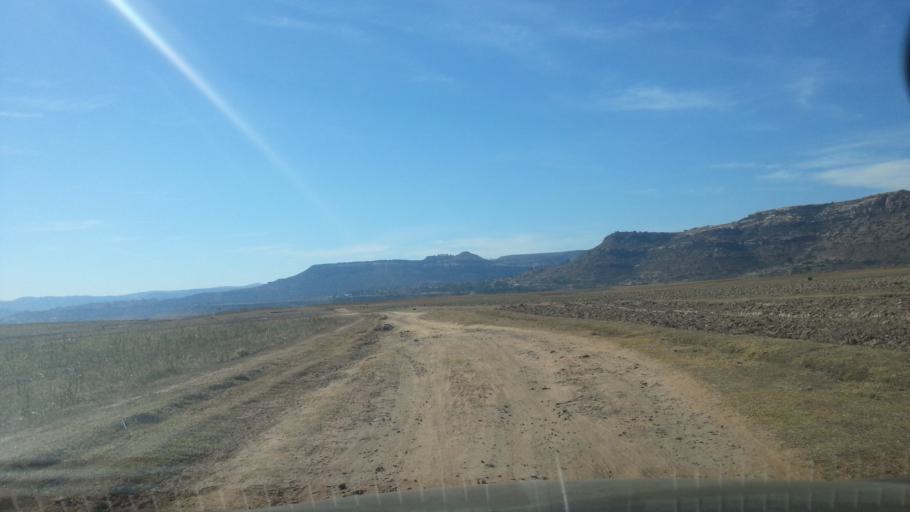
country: LS
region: Maseru
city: Nako
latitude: -29.5119
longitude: 27.6149
